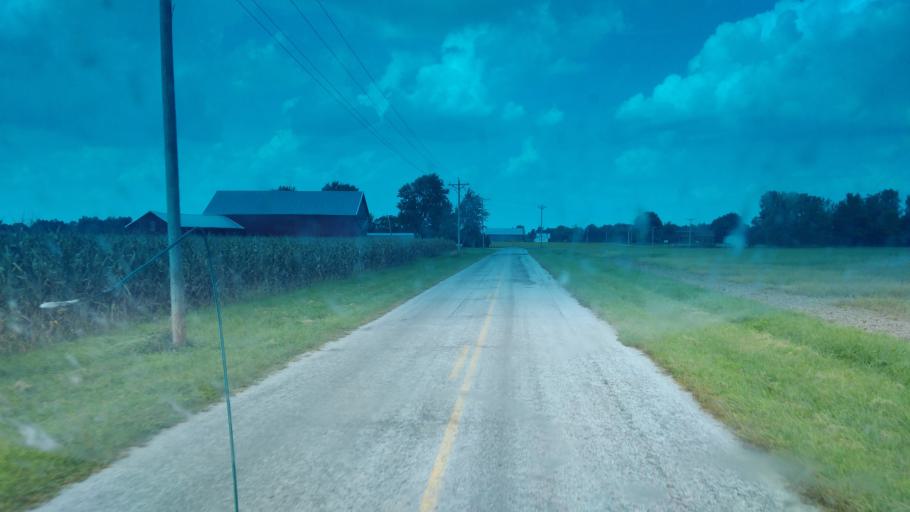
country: US
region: Ohio
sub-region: Hardin County
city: Kenton
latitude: 40.7360
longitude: -83.6021
